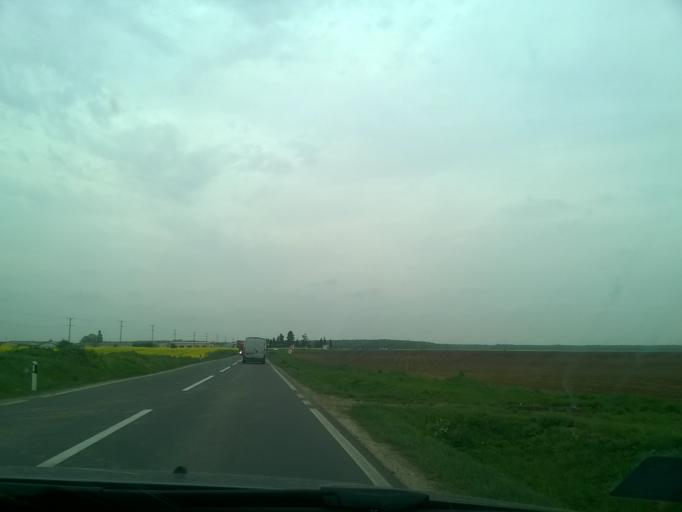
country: RS
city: Hrtkovci
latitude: 44.8538
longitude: 19.7711
